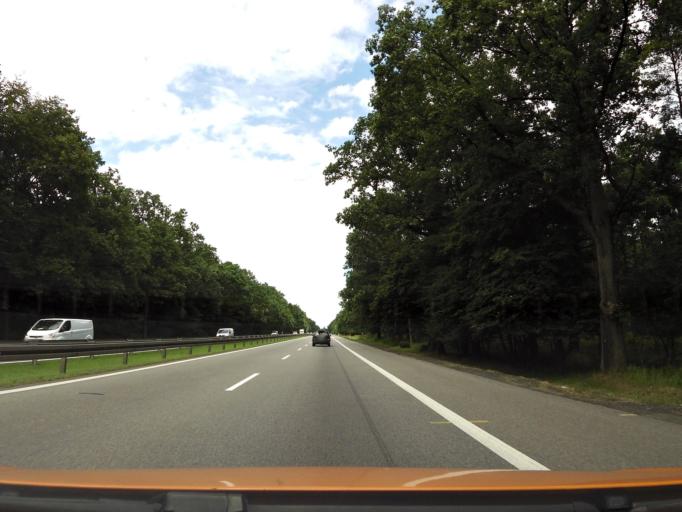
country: PL
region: West Pomeranian Voivodeship
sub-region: Powiat stargardzki
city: Kobylanka
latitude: 53.4379
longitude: 14.7780
